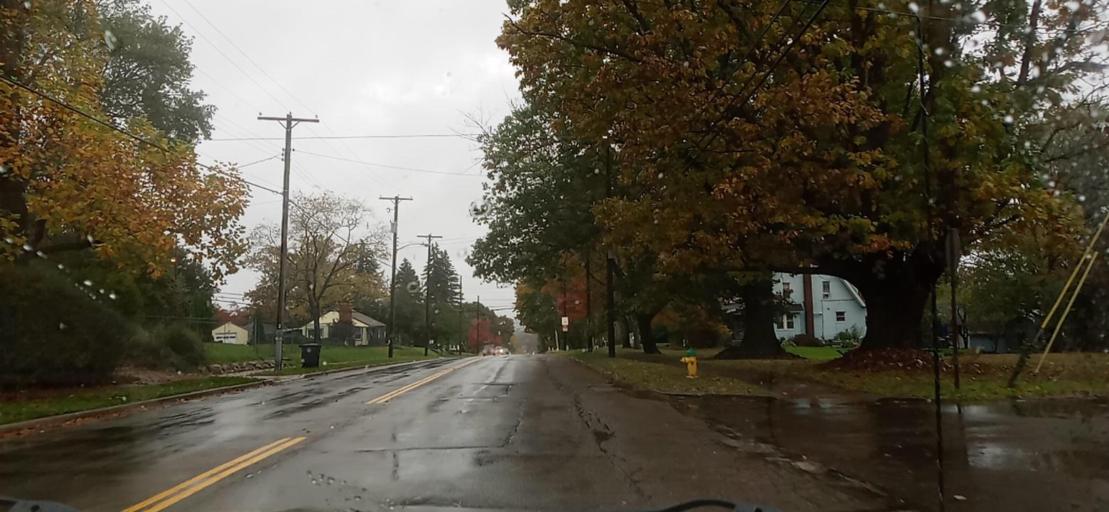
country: US
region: Ohio
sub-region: Summit County
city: Akron
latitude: 41.0553
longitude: -81.5623
